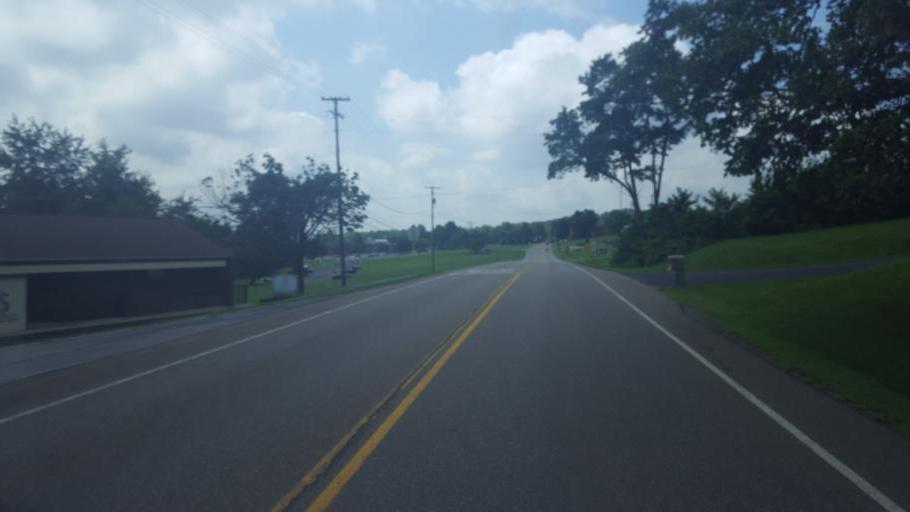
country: US
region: Ohio
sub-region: Fairfield County
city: Lancaster
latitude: 39.7438
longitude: -82.5864
